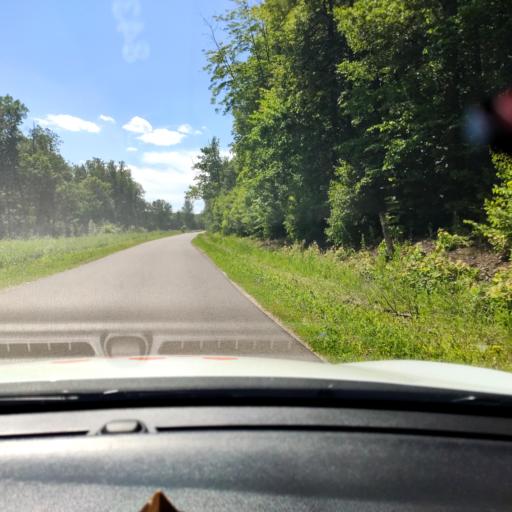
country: RU
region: Tatarstan
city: Sviyazhsk
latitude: 55.7731
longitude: 48.7738
